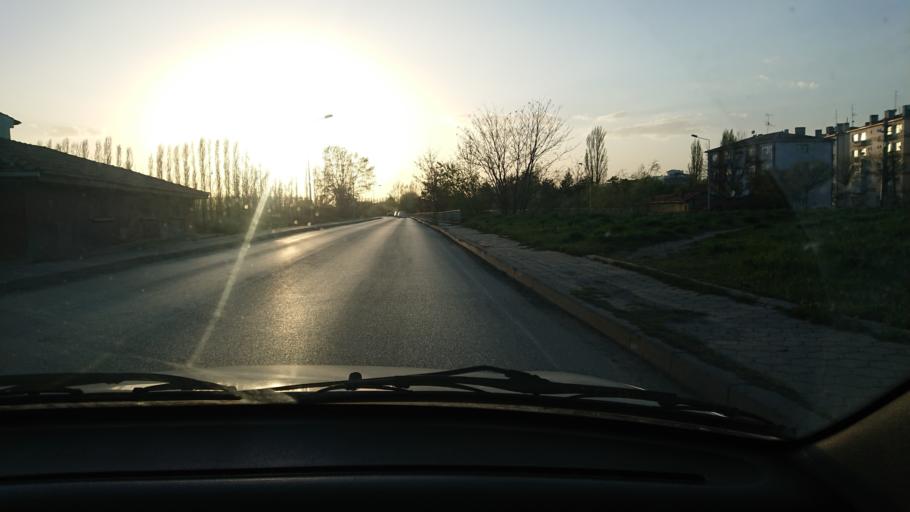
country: TR
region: Eskisehir
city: Eskisehir
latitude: 39.7683
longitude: 30.4801
